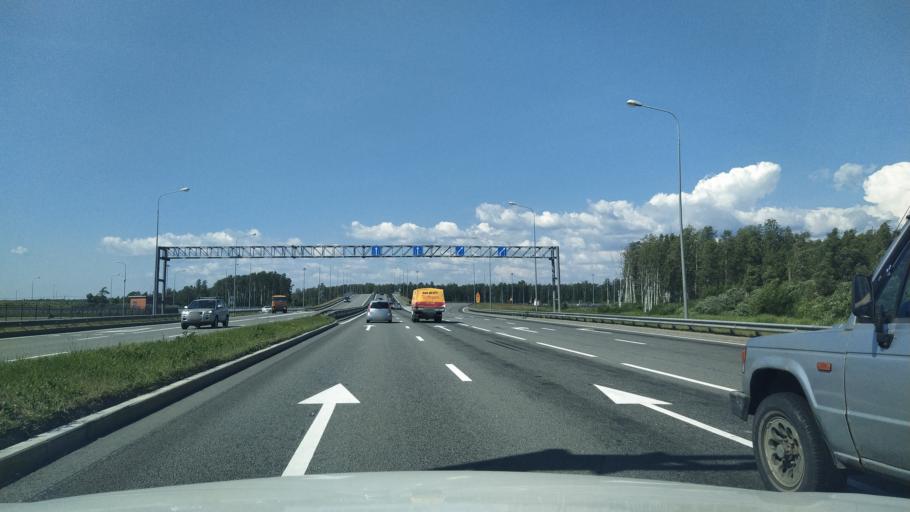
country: RU
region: St.-Petersburg
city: Levashovo
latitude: 60.0721
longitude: 30.1838
